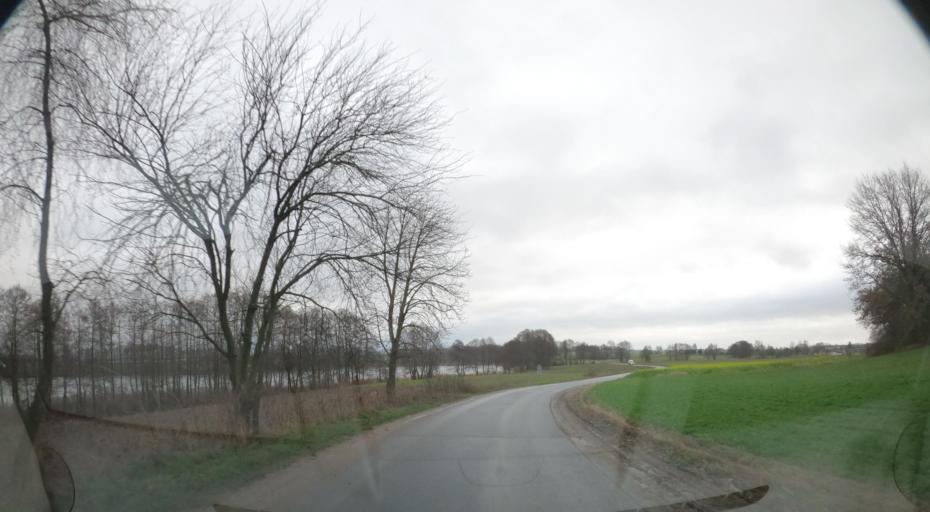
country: PL
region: Greater Poland Voivodeship
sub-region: Powiat pilski
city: Wysoka
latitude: 53.2538
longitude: 17.1416
